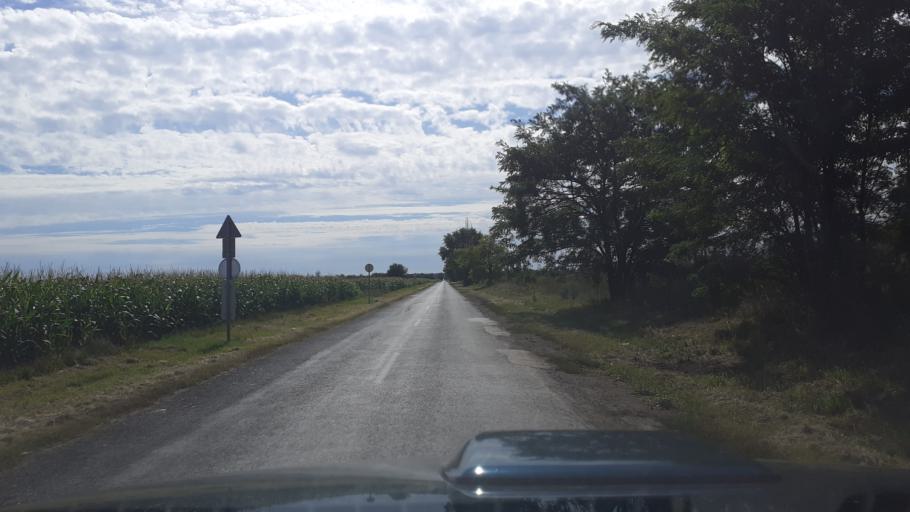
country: HU
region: Fejer
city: Pusztaszabolcs
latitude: 47.1279
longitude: 18.7674
